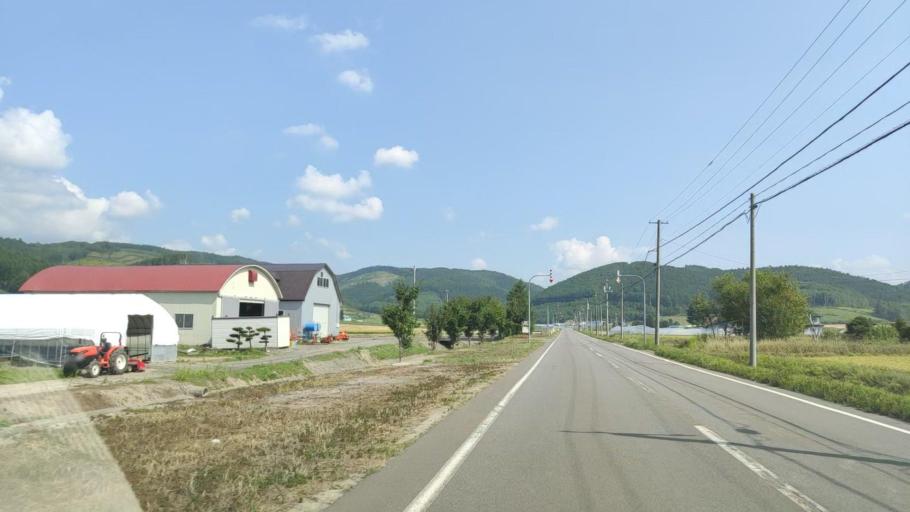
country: JP
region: Hokkaido
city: Shimo-furano
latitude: 43.4117
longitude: 142.3982
